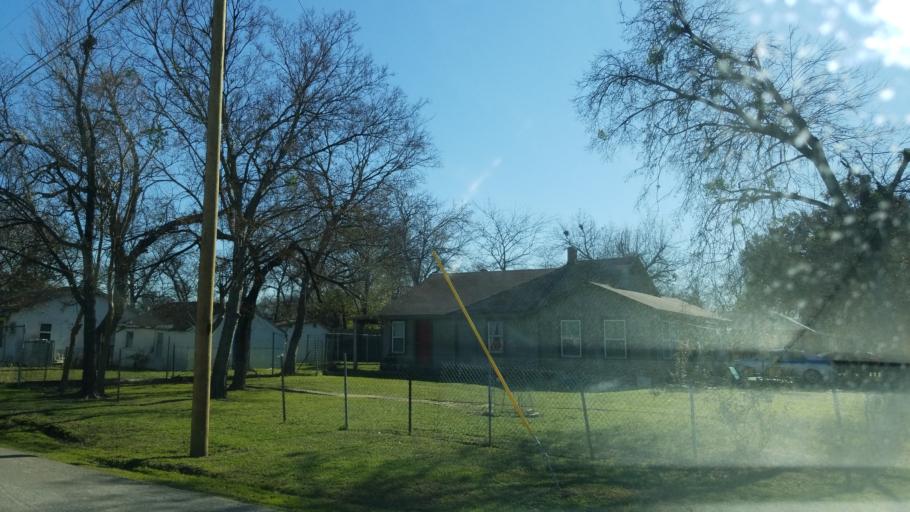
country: US
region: Texas
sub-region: Dallas County
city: Cockrell Hill
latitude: 32.7527
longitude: -96.9153
